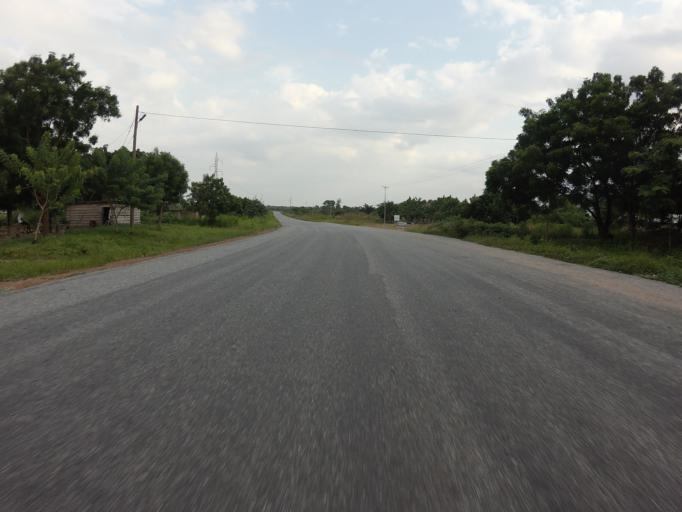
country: GH
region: Volta
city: Ho
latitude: 6.3928
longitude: 0.5261
